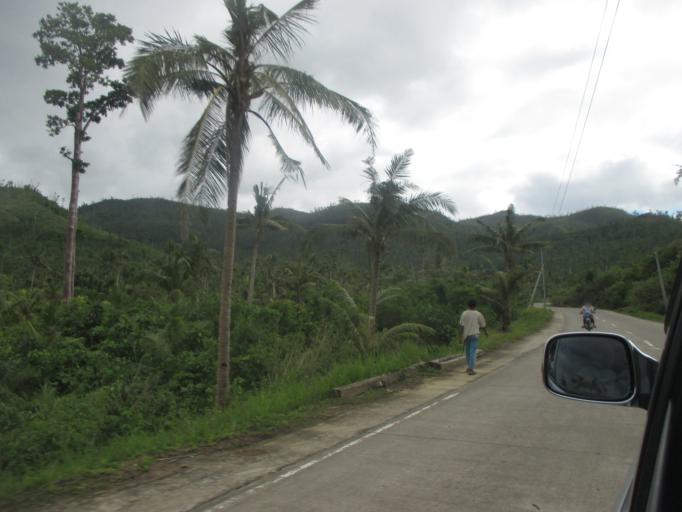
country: PH
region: Eastern Visayas
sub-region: Province of Eastern Samar
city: Lawa-an
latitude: 11.1143
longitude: 125.2107
